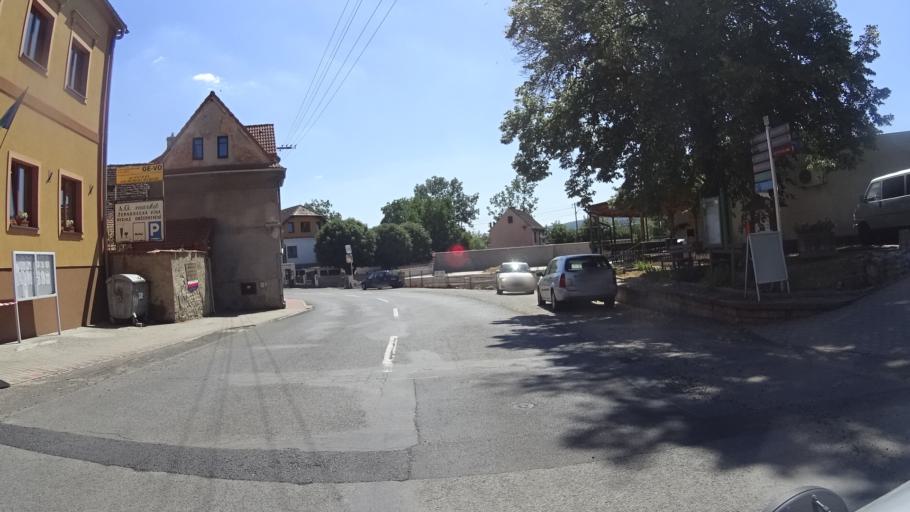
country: CZ
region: Ustecky
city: Lovosice
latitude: 50.5396
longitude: 14.0641
